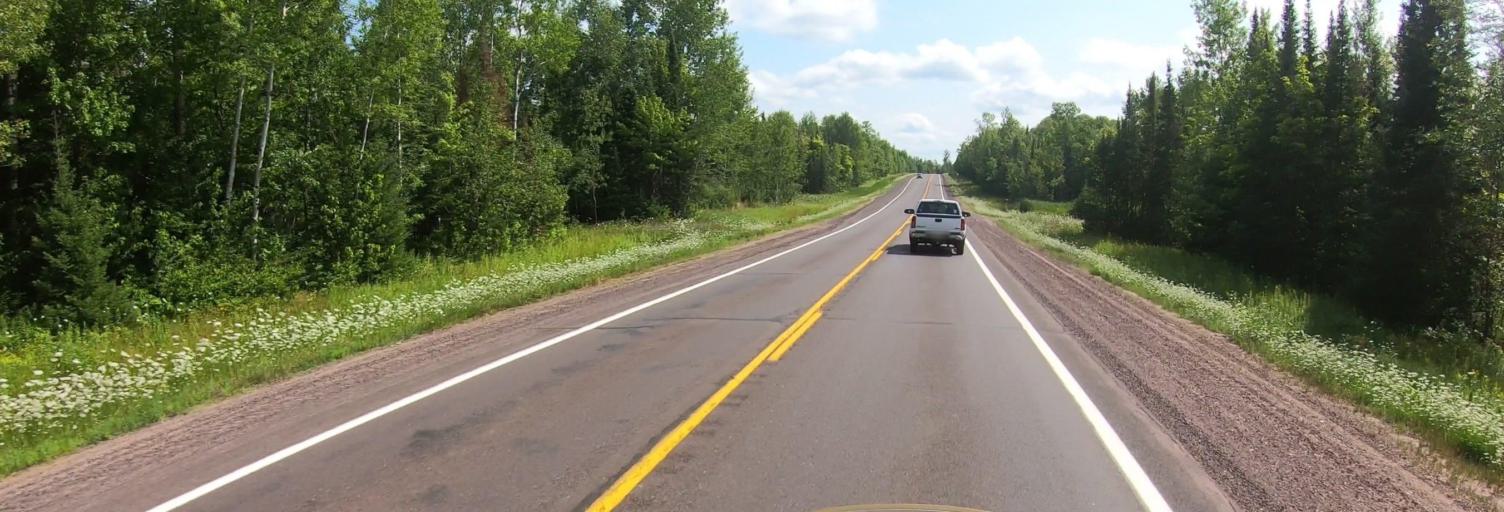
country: US
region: Michigan
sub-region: Ontonagon County
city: Ontonagon
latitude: 46.8153
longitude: -88.9959
